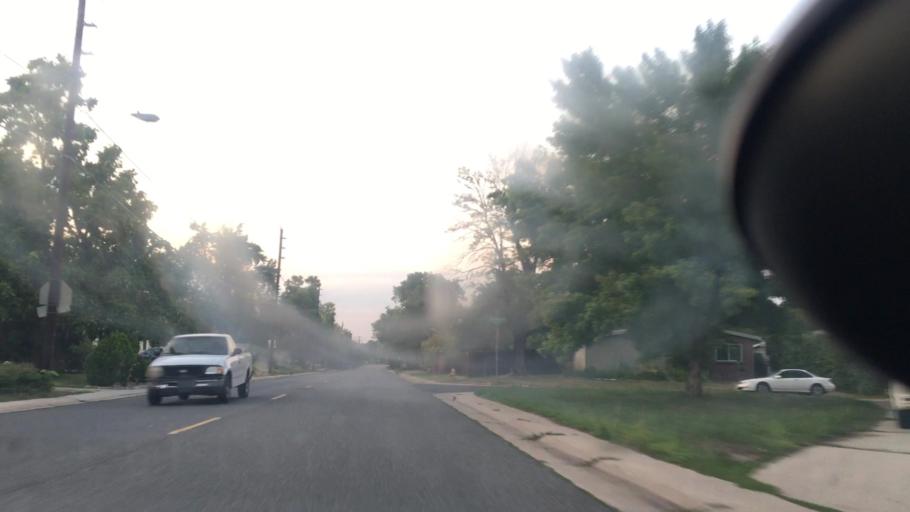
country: US
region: Colorado
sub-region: Arapahoe County
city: Glendale
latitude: 39.6912
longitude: -104.9223
